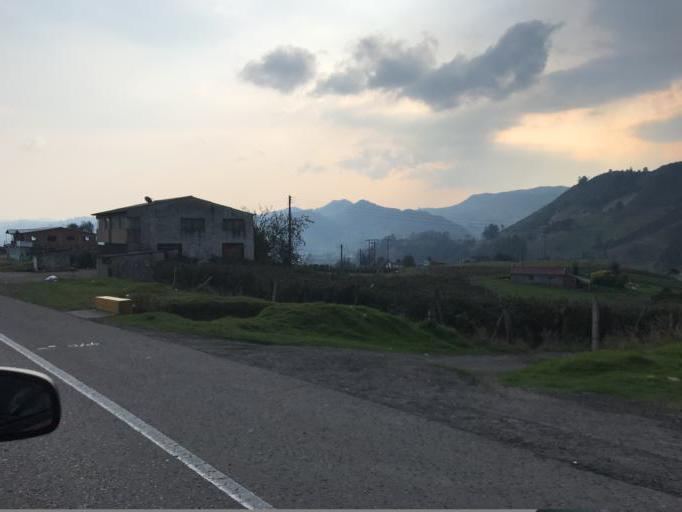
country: CO
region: Boyaca
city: Ventaquemada
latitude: 5.3361
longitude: -73.5602
